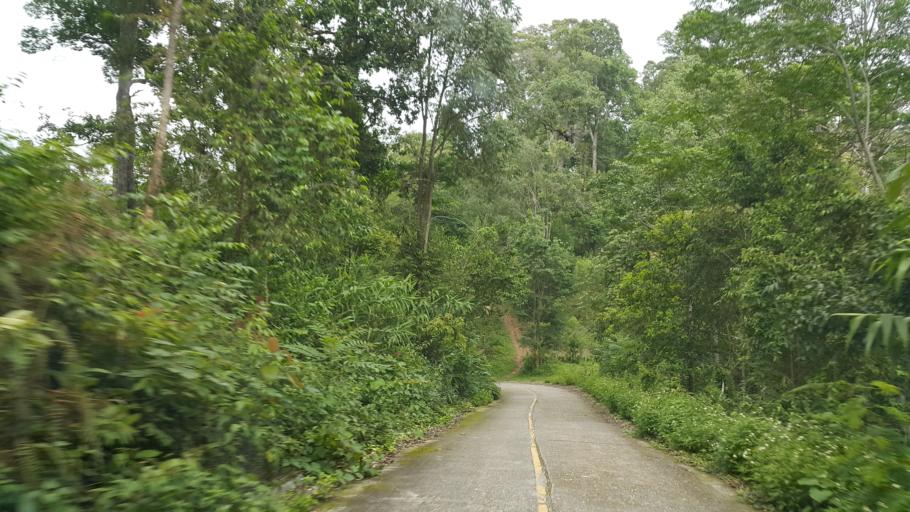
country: TH
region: Lampang
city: Mueang Pan
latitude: 18.8315
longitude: 99.3798
